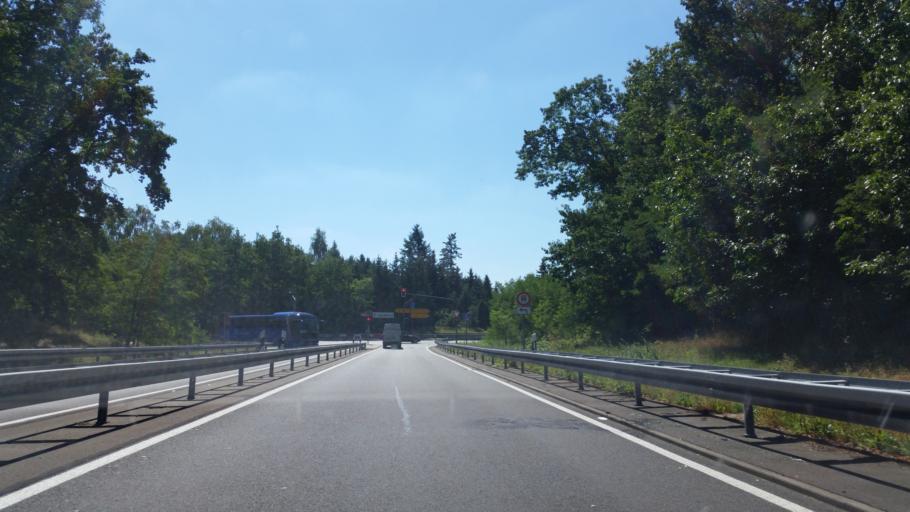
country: DE
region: Brandenburg
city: Cottbus
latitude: 51.7236
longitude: 14.2977
